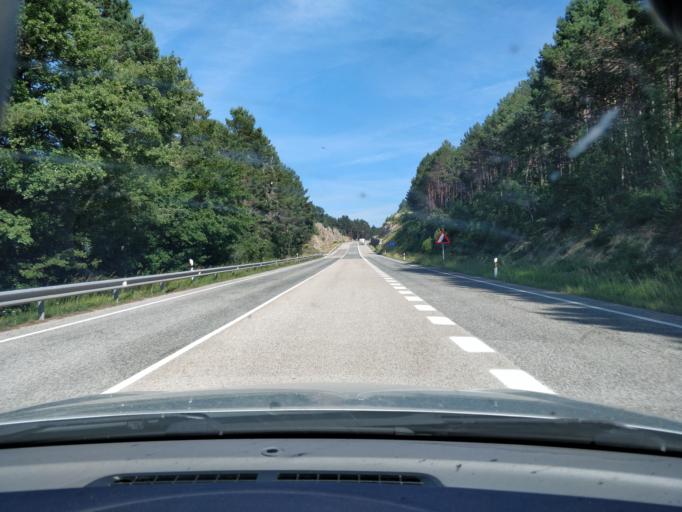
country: ES
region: Cantabria
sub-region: Provincia de Cantabria
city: San Martin de Elines
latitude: 42.9575
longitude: -3.7684
